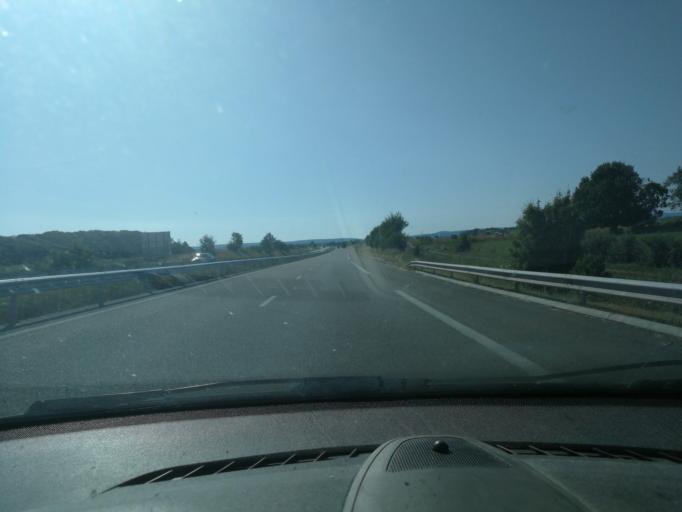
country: FR
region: Alsace
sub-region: Departement du Bas-Rhin
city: Drulingen
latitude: 48.8064
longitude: 7.1753
